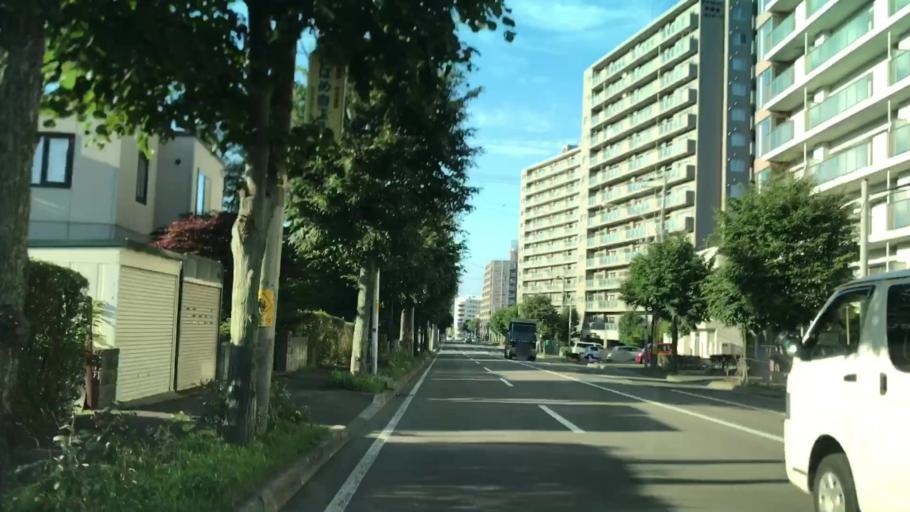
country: JP
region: Hokkaido
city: Sapporo
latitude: 43.0460
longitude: 141.3641
